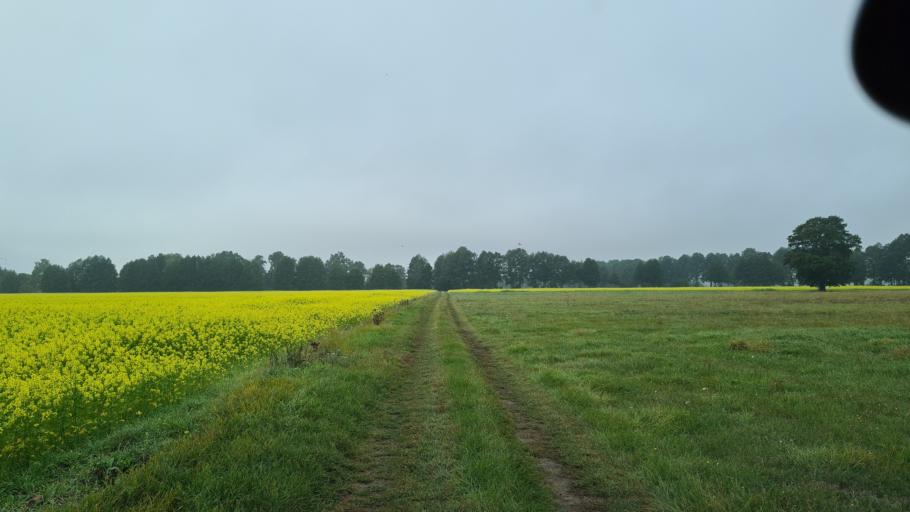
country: DE
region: Brandenburg
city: Schonewalde
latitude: 51.6580
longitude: 13.6089
